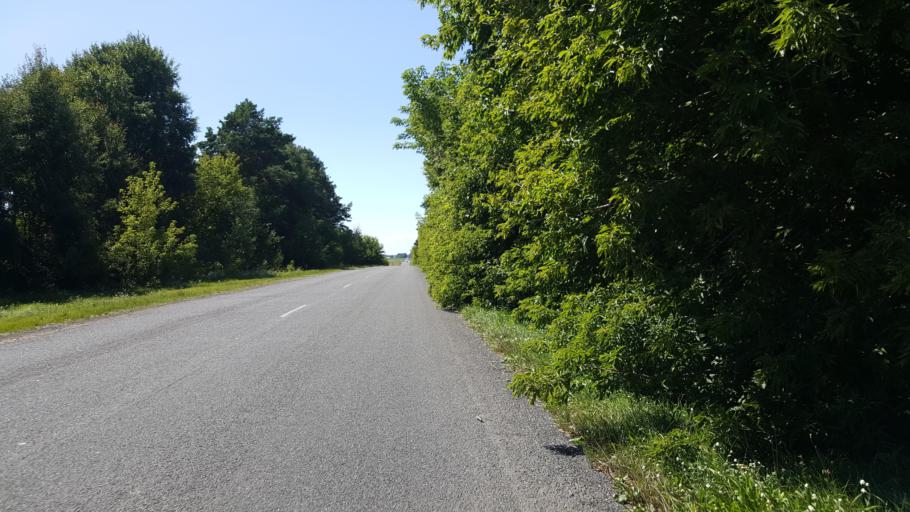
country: BY
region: Brest
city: Charnawchytsy
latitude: 52.2061
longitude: 23.8035
